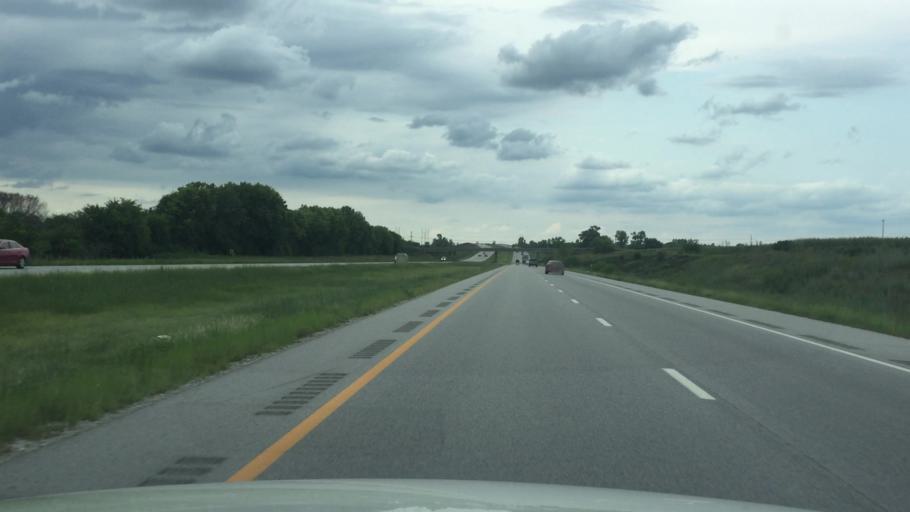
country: US
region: Kansas
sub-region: Miami County
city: Louisburg
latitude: 38.7340
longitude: -94.6763
